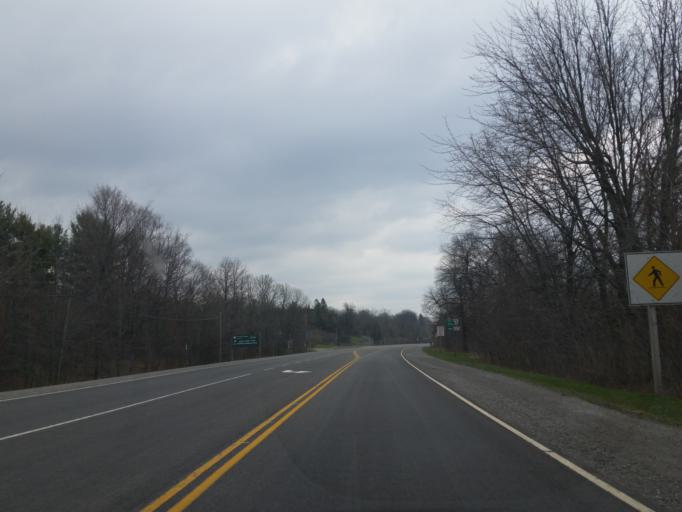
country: US
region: New York
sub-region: Jefferson County
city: Alexandria Bay
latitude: 44.4532
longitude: -75.8607
